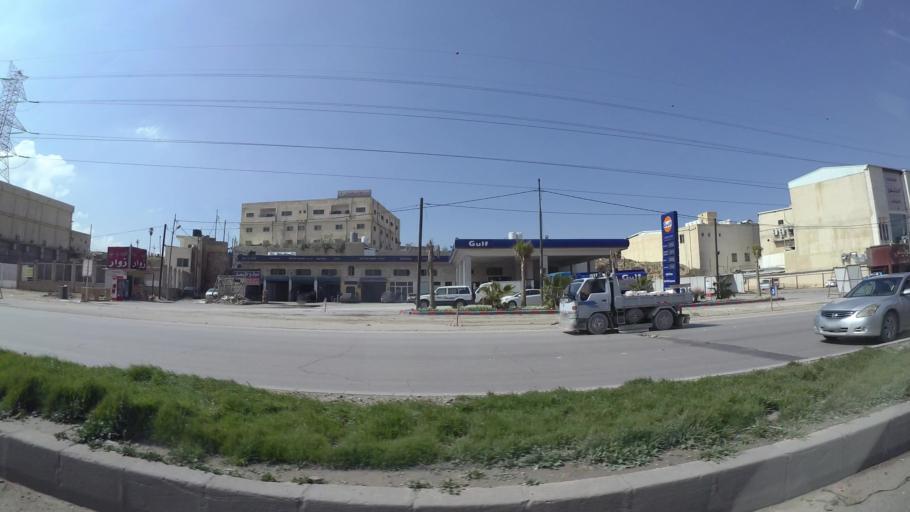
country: JO
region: Zarqa
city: Russeifa
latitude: 32.0030
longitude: 36.0372
